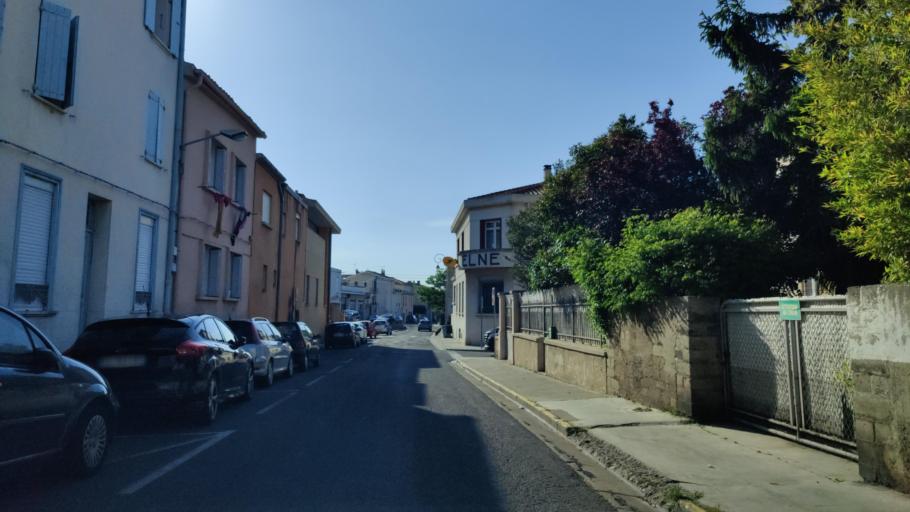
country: FR
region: Languedoc-Roussillon
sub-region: Departement des Pyrenees-Orientales
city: Elne
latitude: 42.6012
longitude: 2.9717
